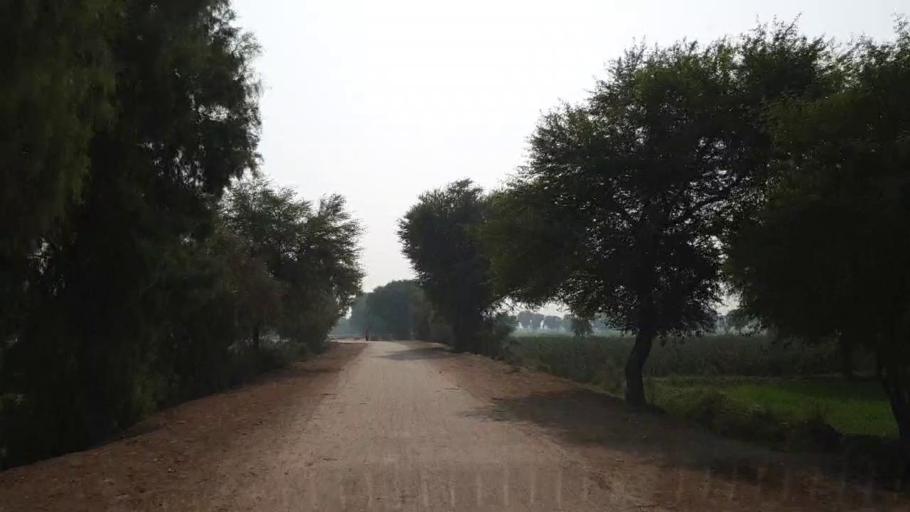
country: PK
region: Sindh
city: Bhan
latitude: 26.5195
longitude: 67.7322
